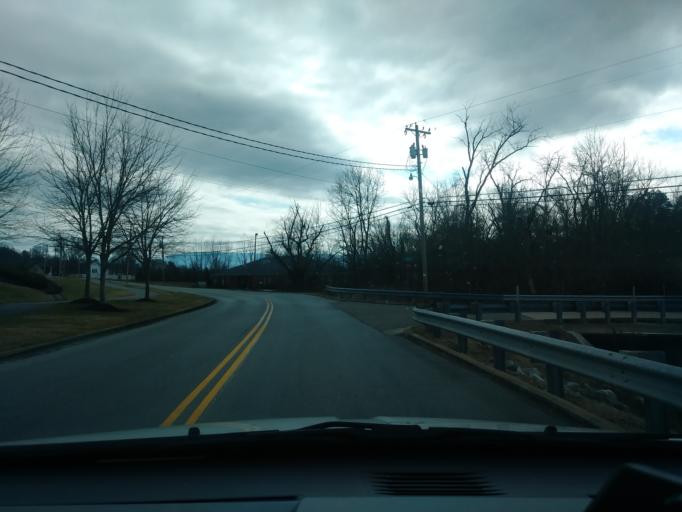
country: US
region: Tennessee
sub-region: Greene County
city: Tusculum
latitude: 36.1728
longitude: -82.7936
